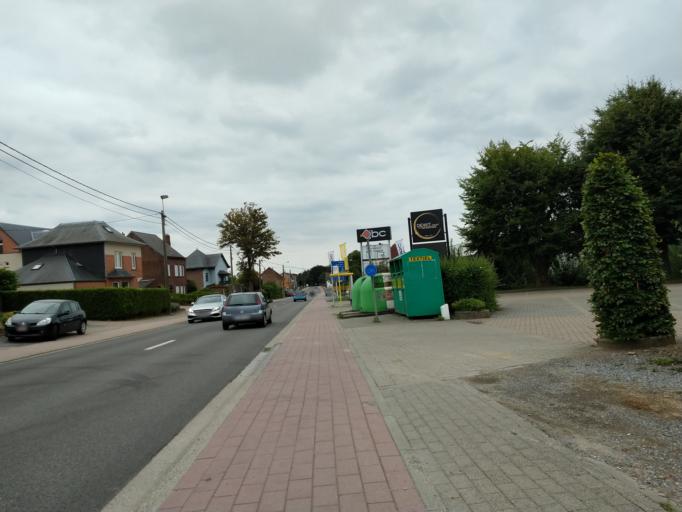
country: BE
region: Flanders
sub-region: Provincie Vlaams-Brabant
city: Overijse
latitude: 50.7797
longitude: 4.5174
